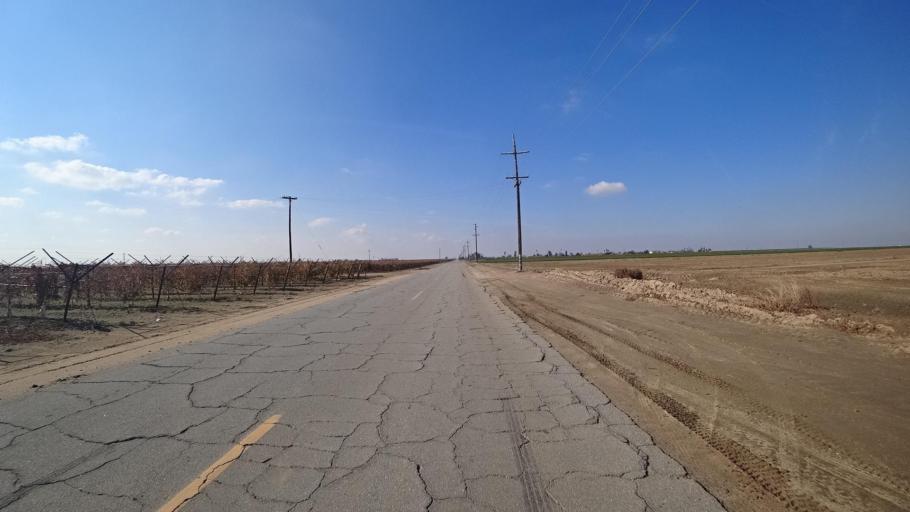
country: US
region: California
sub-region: Kern County
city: Arvin
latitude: 35.2238
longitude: -118.8106
